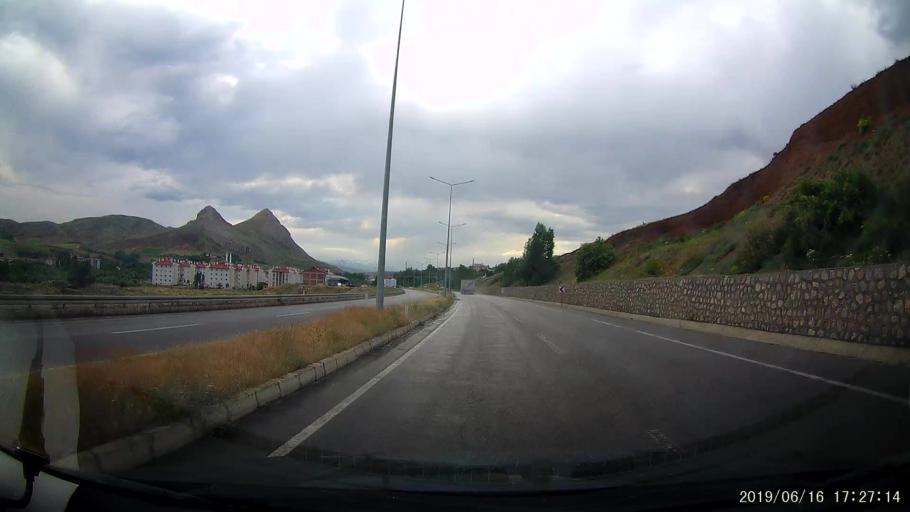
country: TR
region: Erzincan
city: Tercan
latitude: 39.7756
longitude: 40.3971
